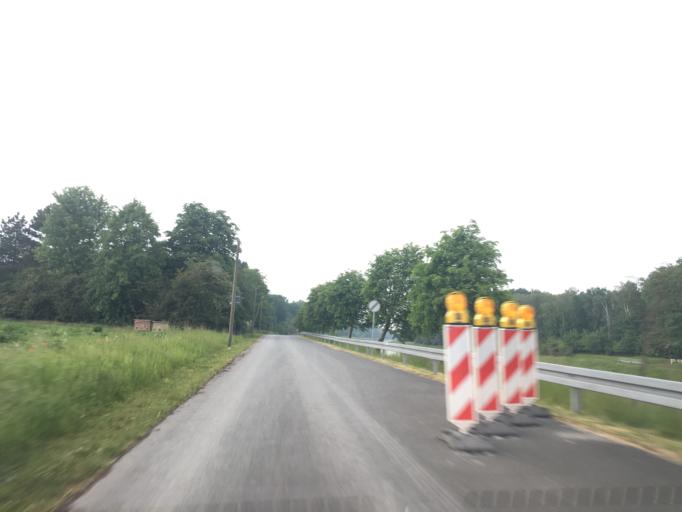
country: DE
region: North Rhine-Westphalia
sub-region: Regierungsbezirk Munster
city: Muenster
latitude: 52.0006
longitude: 7.6587
